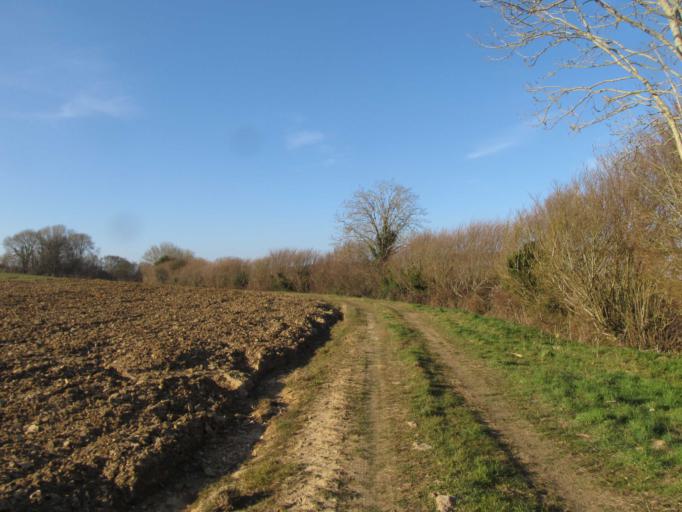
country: GB
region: England
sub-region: West Sussex
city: Petworth
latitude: 50.9740
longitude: -0.6306
